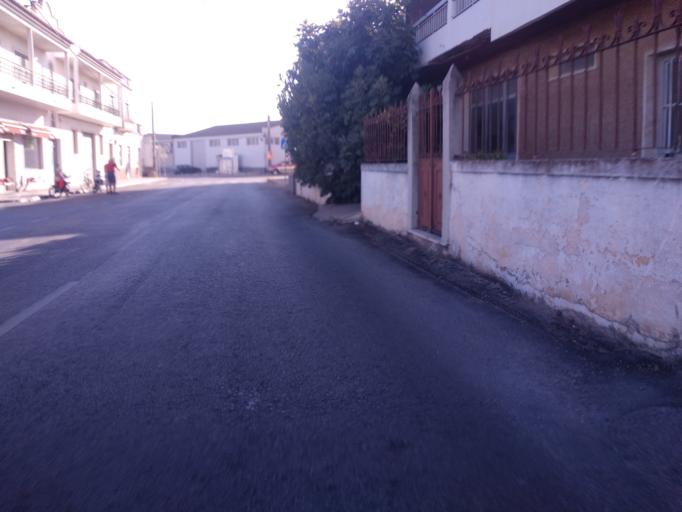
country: PT
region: Faro
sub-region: Faro
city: Faro
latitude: 37.0508
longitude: -7.9371
